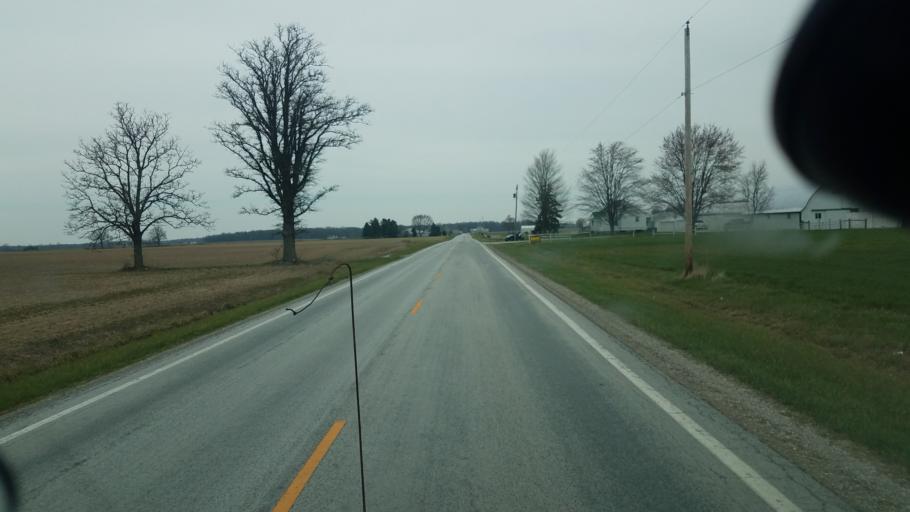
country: US
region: Ohio
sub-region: Hardin County
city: Forest
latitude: 40.8808
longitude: -83.5247
